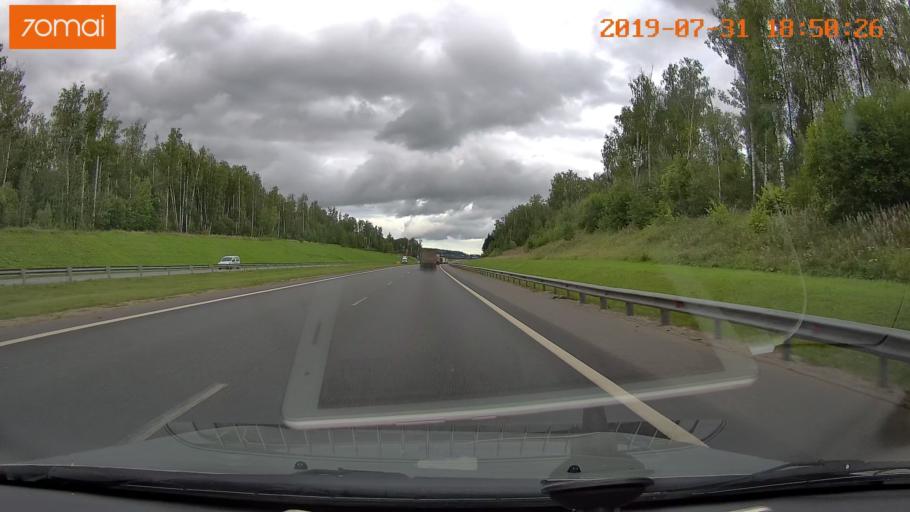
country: RU
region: Moskovskaya
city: Troitskoye
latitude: 55.2287
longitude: 38.5820
